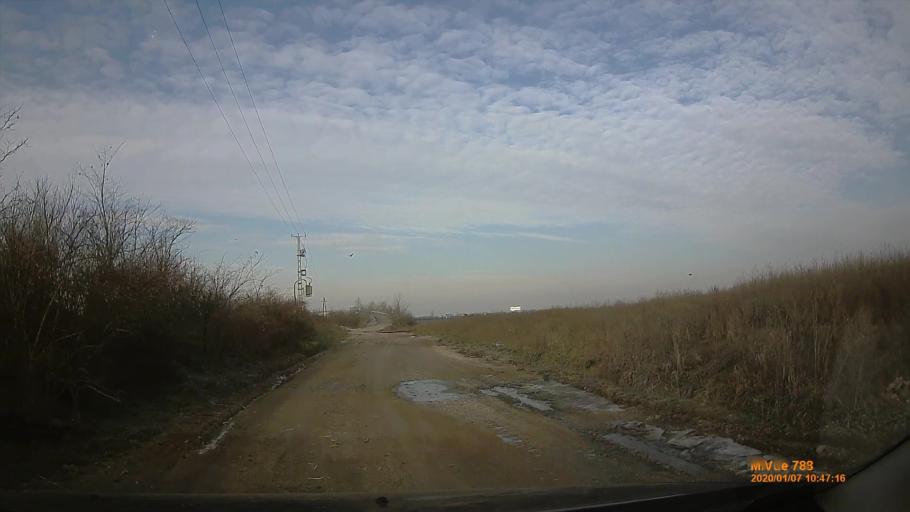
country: HU
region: Gyor-Moson-Sopron
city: Rajka
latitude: 47.9128
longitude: 17.1842
